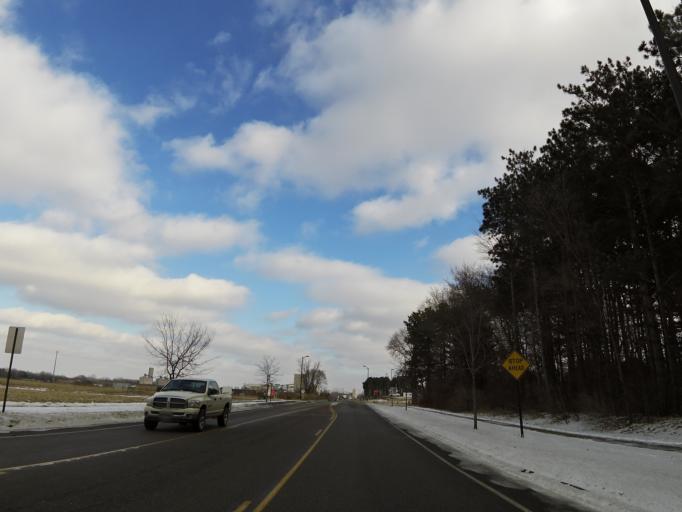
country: US
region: Minnesota
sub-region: Scott County
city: Shakopee
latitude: 44.7974
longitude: -93.4922
